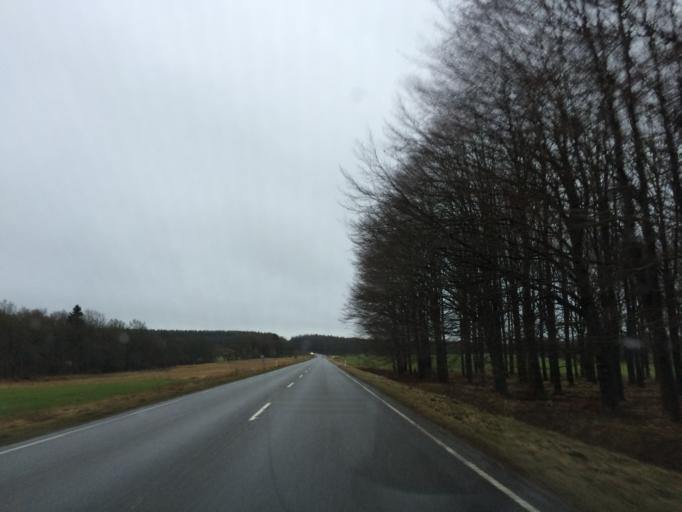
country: DK
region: North Denmark
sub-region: Mariagerfjord Kommune
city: Arden
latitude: 56.8105
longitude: 9.8186
